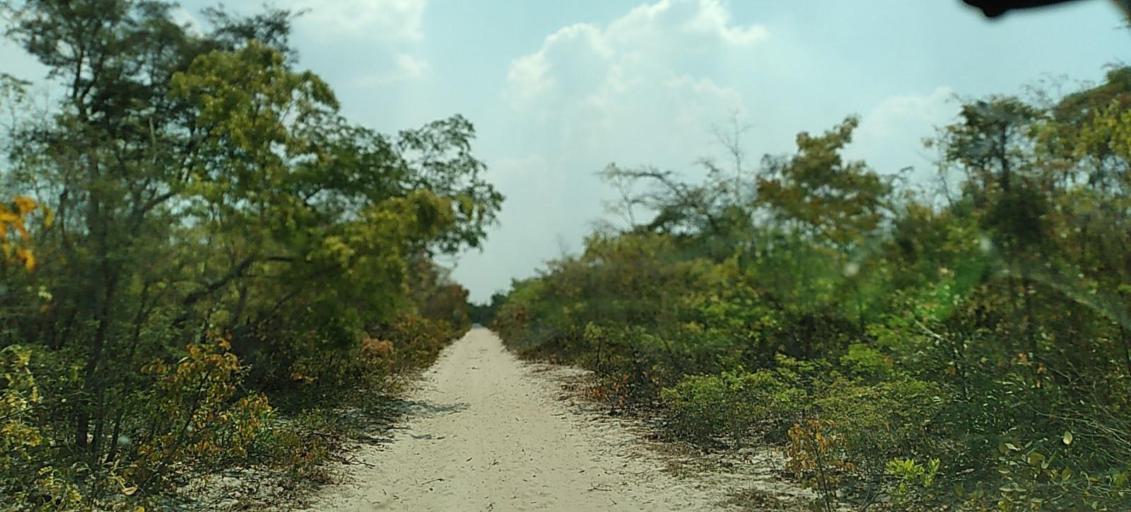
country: ZM
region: North-Western
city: Kabompo
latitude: -13.4010
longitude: 23.8150
